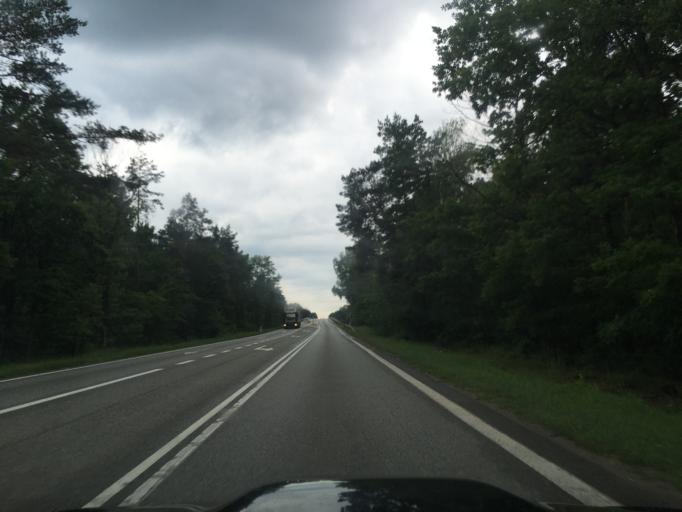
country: PL
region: Masovian Voivodeship
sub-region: Powiat otwocki
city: Celestynow
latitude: 52.0462
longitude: 21.4246
